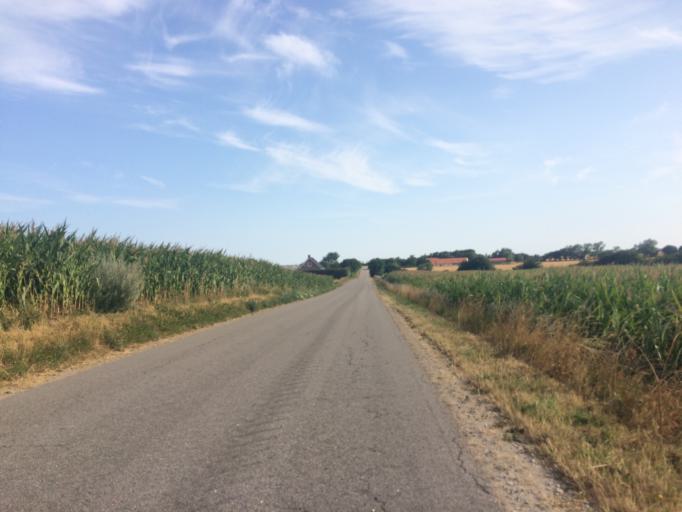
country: DK
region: Central Jutland
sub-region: Holstebro Kommune
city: Vinderup
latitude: 56.5704
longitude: 8.7570
